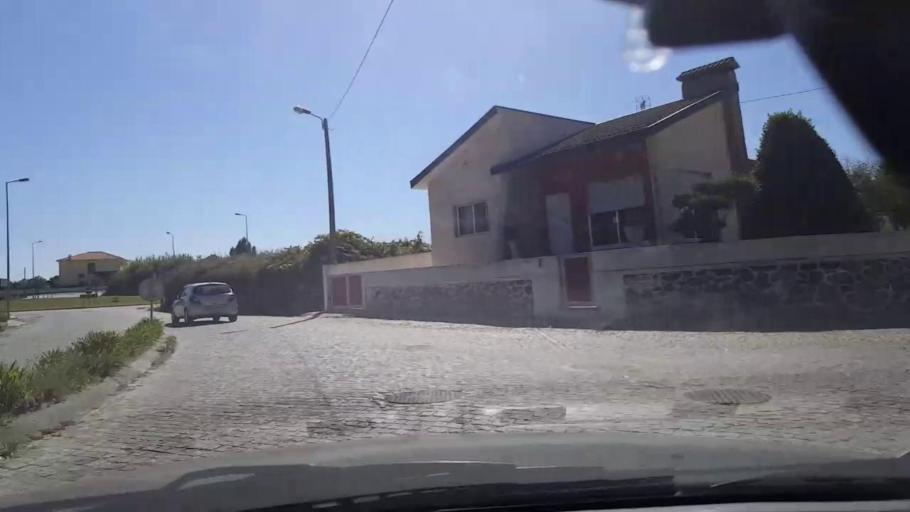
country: PT
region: Porto
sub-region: Vila do Conde
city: Arvore
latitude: 41.3183
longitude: -8.7233
